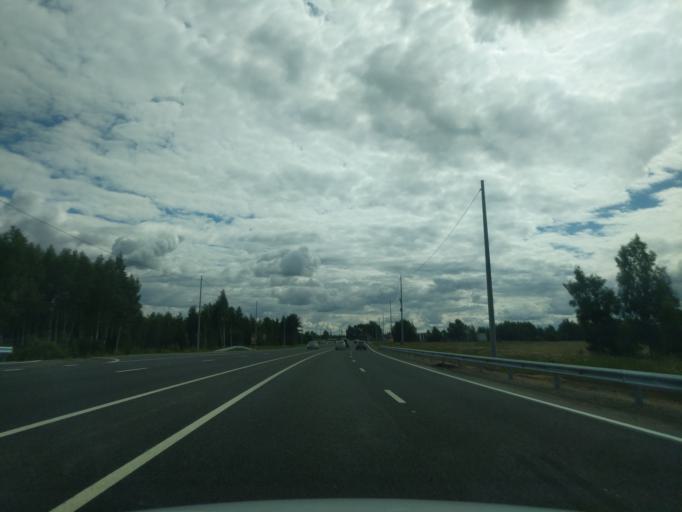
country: RU
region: Kostroma
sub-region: Kostromskoy Rayon
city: Kostroma
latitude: 57.7370
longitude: 40.8666
